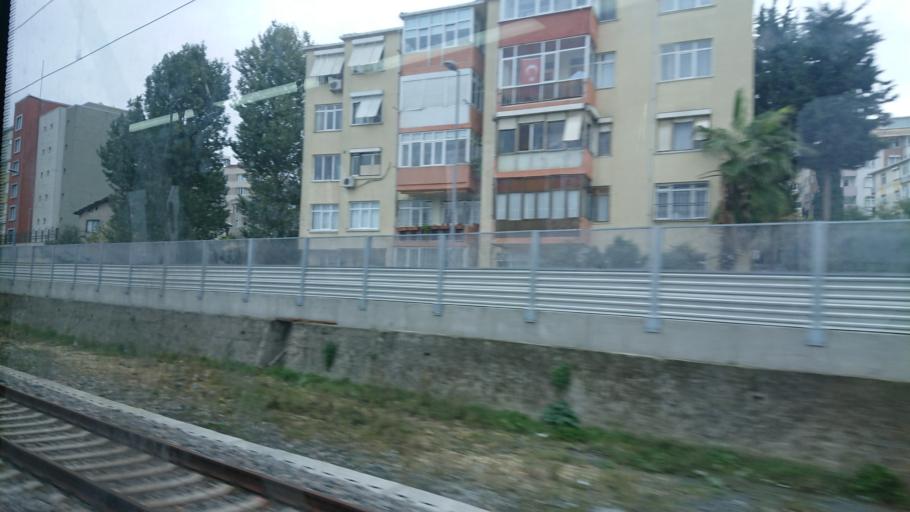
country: TR
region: Istanbul
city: Mahmutbey
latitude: 41.0017
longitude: 28.7691
